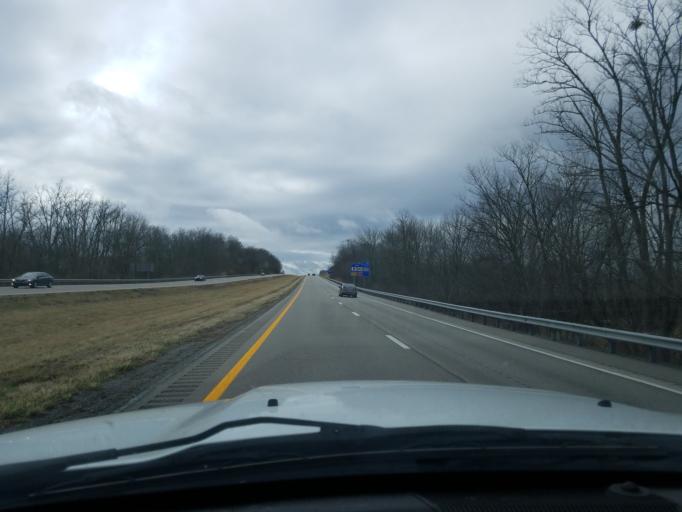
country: US
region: Kentucky
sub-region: Montgomery County
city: Mount Sterling
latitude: 38.0827
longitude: -83.9340
